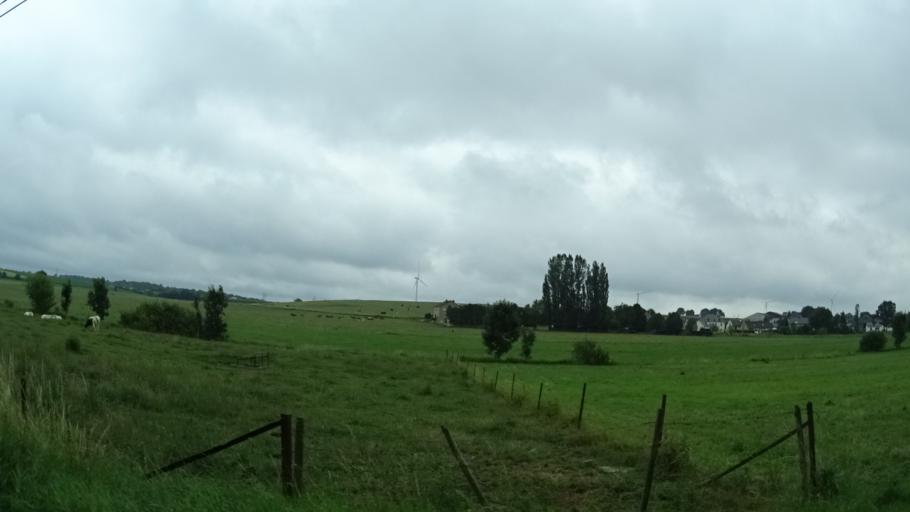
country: LU
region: Luxembourg
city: Eischen
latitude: 49.6493
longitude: 5.8730
